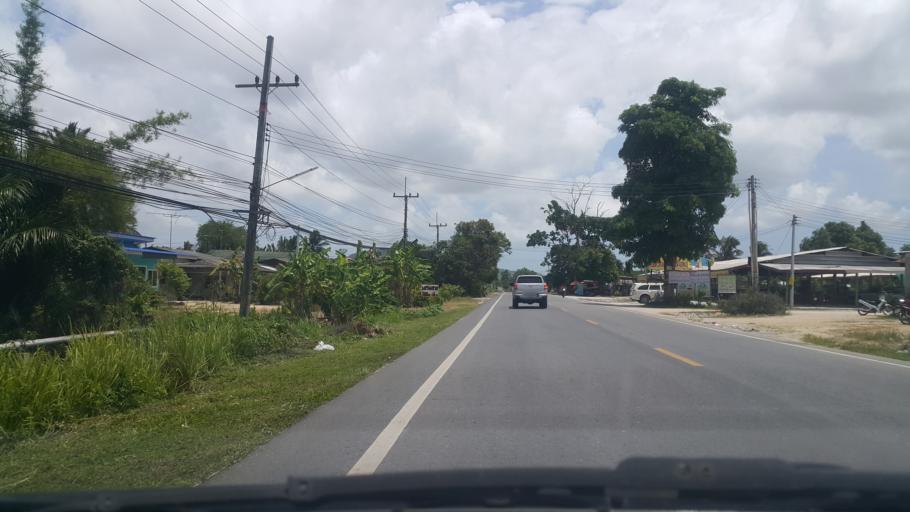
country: TH
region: Rayong
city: Ban Chang
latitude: 12.7598
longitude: 101.0266
